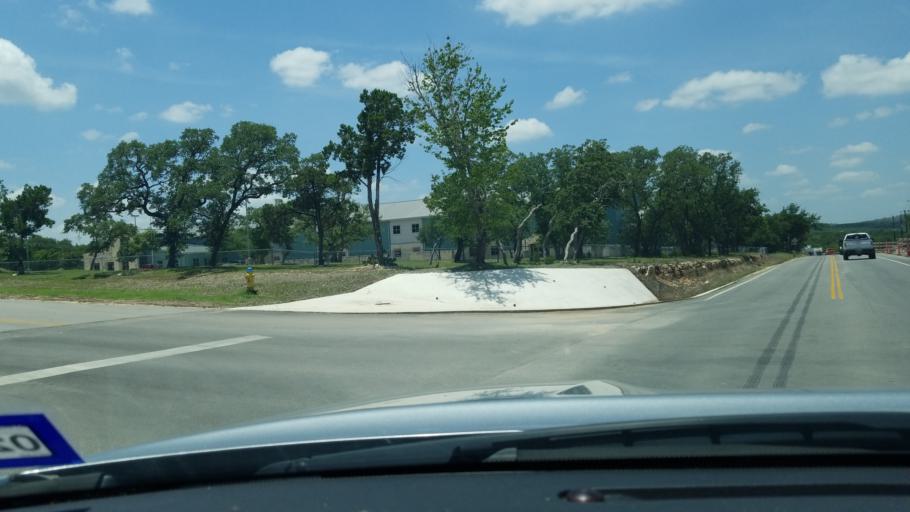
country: US
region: Texas
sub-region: Bexar County
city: Timberwood Park
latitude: 29.7081
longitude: -98.5096
